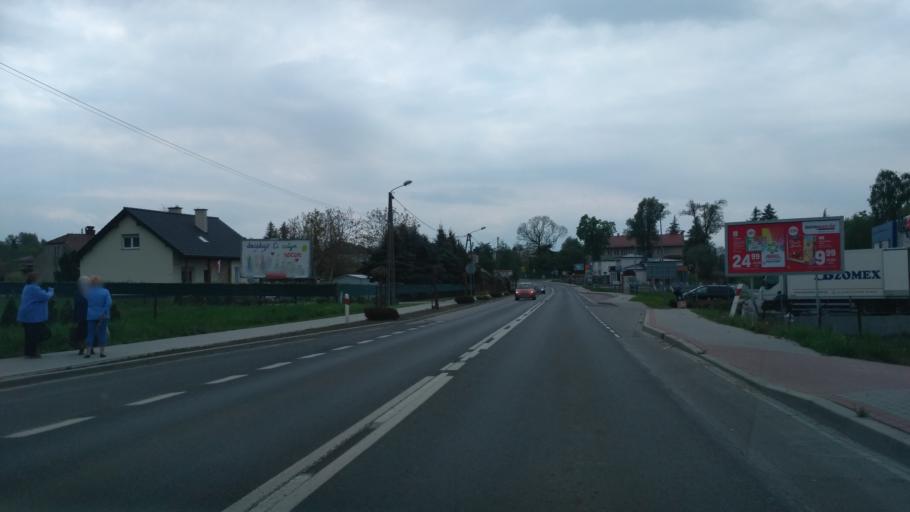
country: PL
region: Lesser Poland Voivodeship
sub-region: Powiat tarnowski
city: Tarnowiec
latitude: 49.9860
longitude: 20.9852
